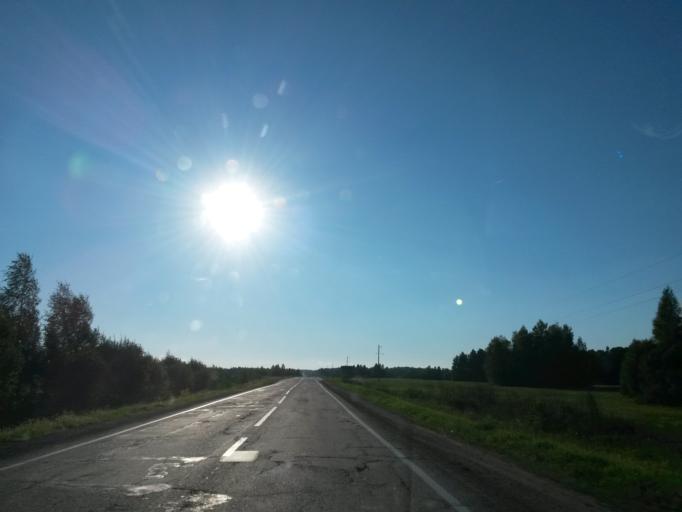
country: RU
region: Jaroslavl
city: Gavrilov-Yam
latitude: 57.2617
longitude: 40.0420
